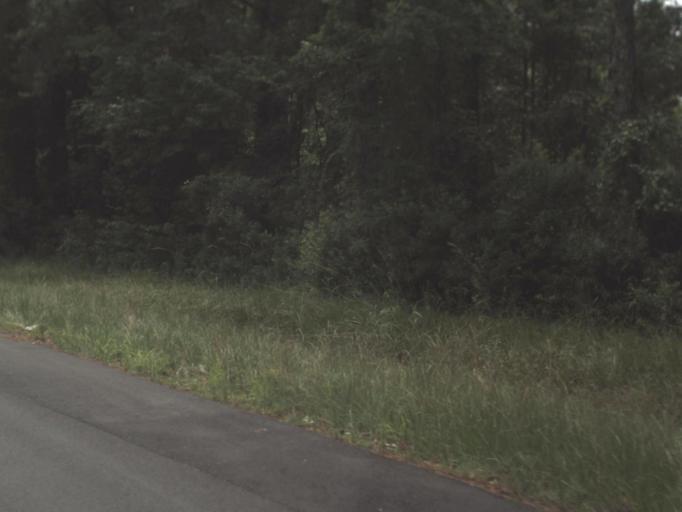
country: US
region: Florida
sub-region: Jefferson County
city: Monticello
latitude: 30.4838
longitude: -83.6920
